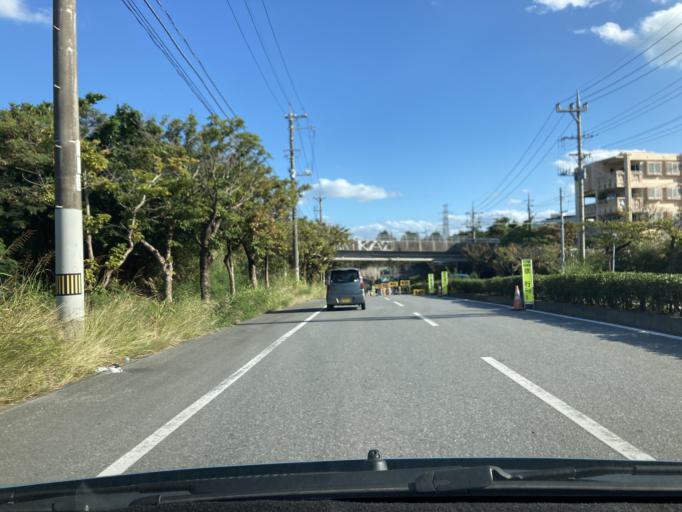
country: JP
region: Okinawa
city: Gushikawa
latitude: 26.3466
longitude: 127.8355
